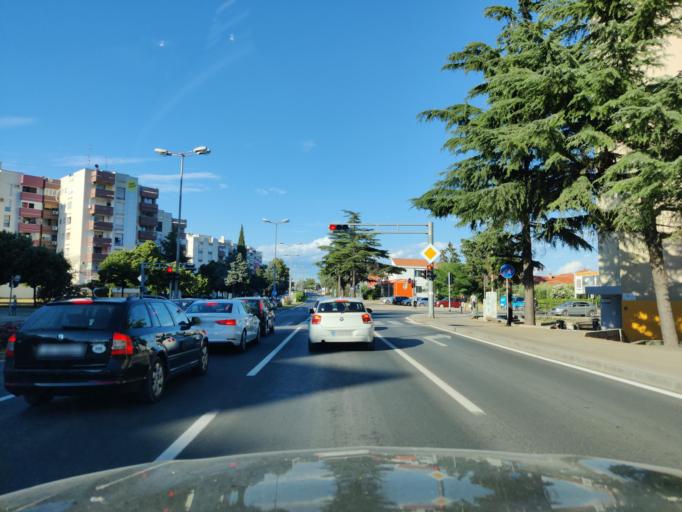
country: HR
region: Zadarska
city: Zadar
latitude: 44.1086
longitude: 15.2450
